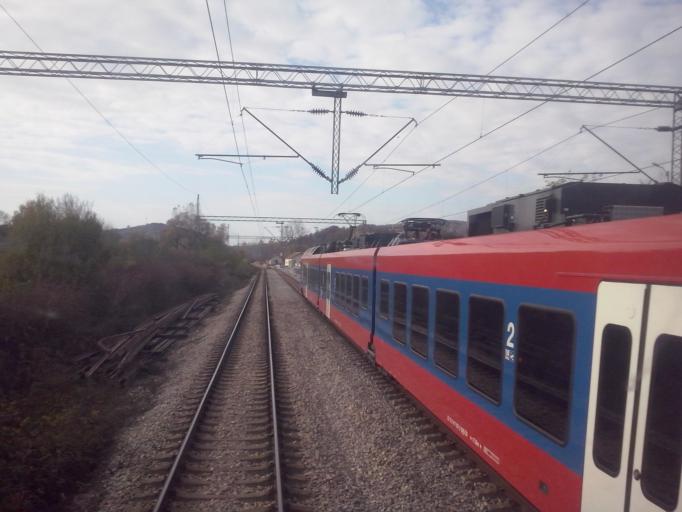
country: RS
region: Central Serbia
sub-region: Kolubarski Okrug
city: Lajkovac
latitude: 44.3497
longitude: 20.0962
